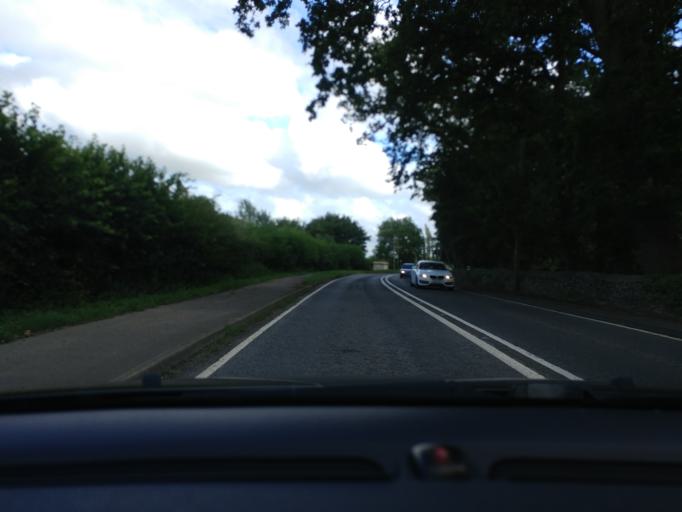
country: GB
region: England
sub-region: Oxfordshire
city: Kidlington
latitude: 51.8633
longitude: -1.2253
